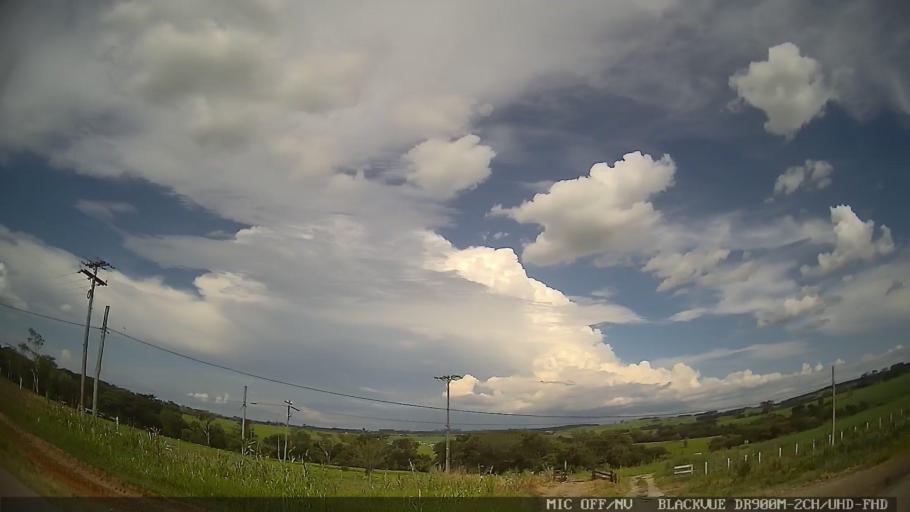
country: BR
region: Sao Paulo
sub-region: Conchas
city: Conchas
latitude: -23.0498
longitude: -47.9584
